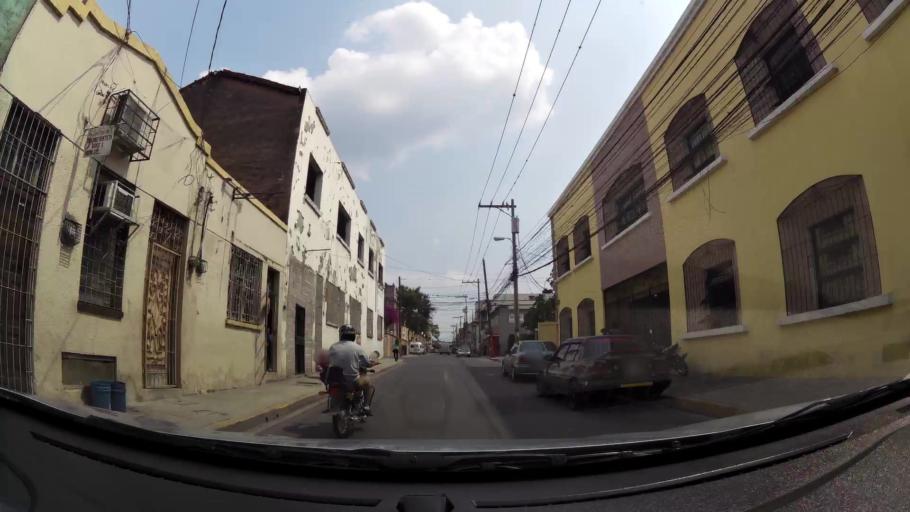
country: HN
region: Francisco Morazan
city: Tegucigalpa
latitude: 14.1077
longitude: -87.2093
